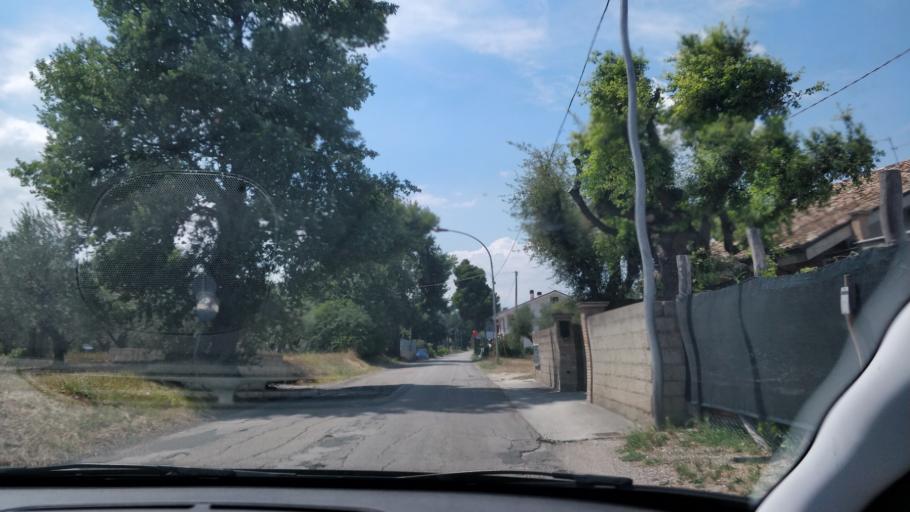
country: IT
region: Abruzzo
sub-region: Provincia di Chieti
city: Torrevecchia
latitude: 42.3953
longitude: 14.2050
